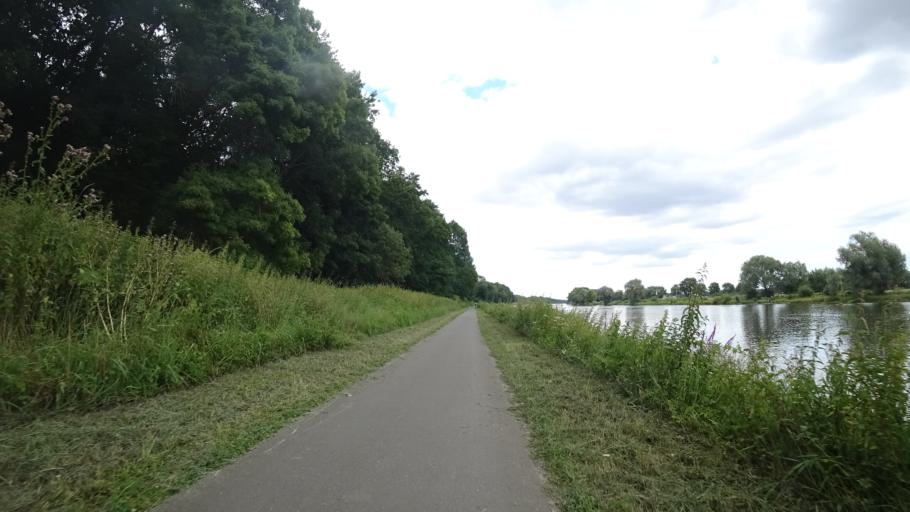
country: DE
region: North Rhine-Westphalia
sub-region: Regierungsbezirk Detmold
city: Minden
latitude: 52.3197
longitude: 8.9219
